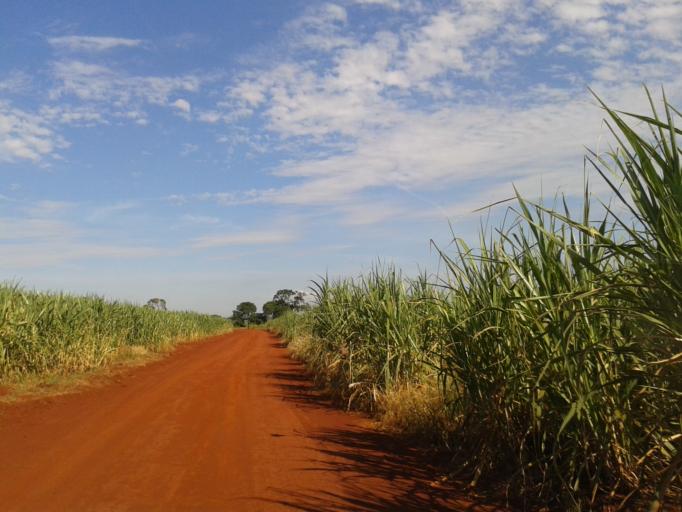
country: BR
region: Minas Gerais
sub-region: Centralina
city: Centralina
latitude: -18.6357
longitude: -49.2474
